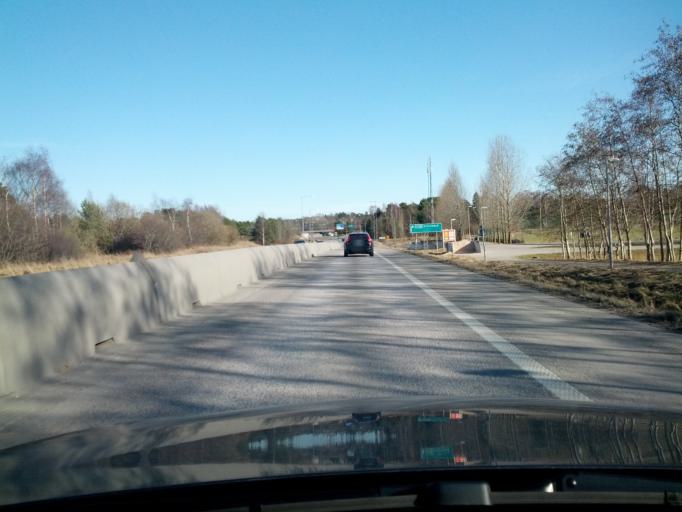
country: SE
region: Stockholm
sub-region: Upplands Vasby Kommun
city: Upplands Vaesby
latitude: 59.4720
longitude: 17.9022
